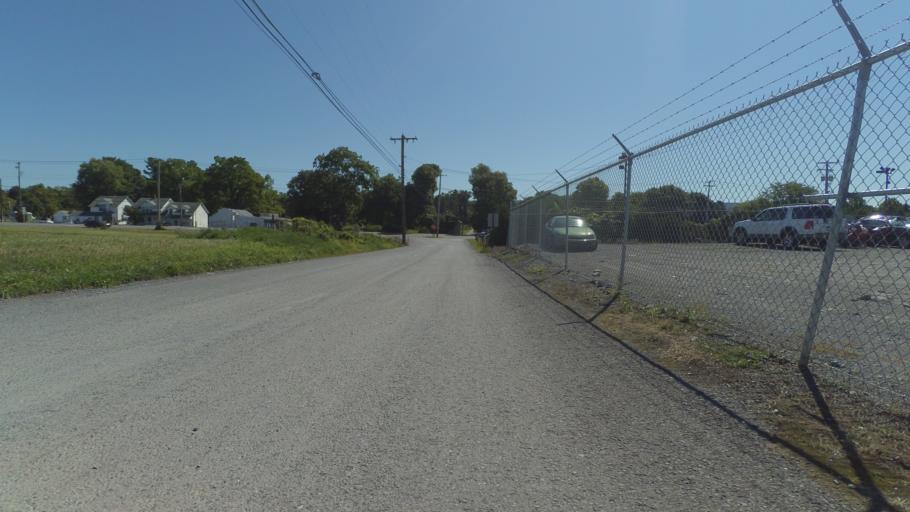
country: US
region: Pennsylvania
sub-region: Centre County
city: State College
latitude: 40.7794
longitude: -77.8819
